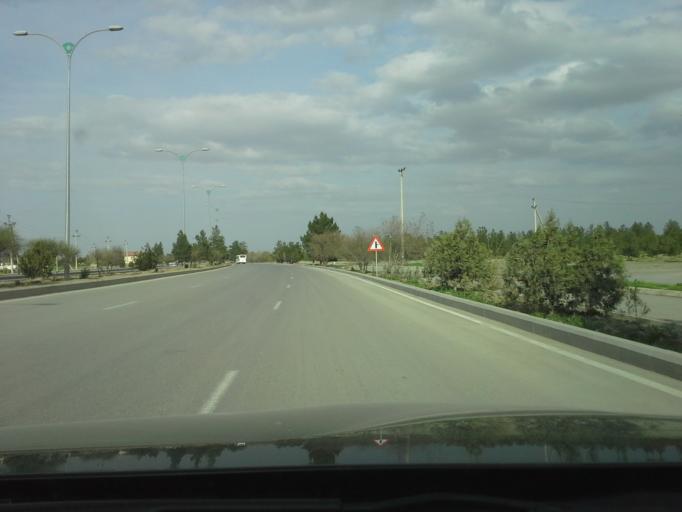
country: TM
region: Ahal
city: Abadan
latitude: 37.9666
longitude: 58.2273
